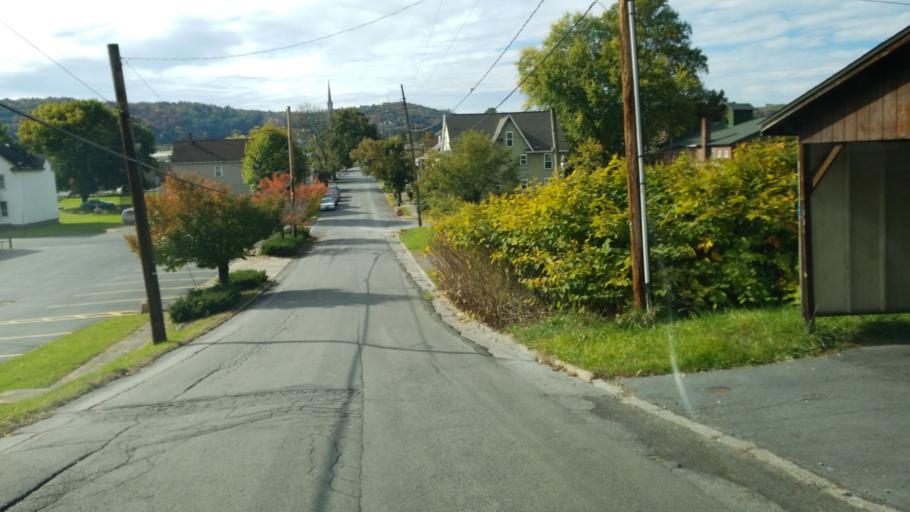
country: US
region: Pennsylvania
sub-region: Clearfield County
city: Clearfield
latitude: 41.0244
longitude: -78.4337
